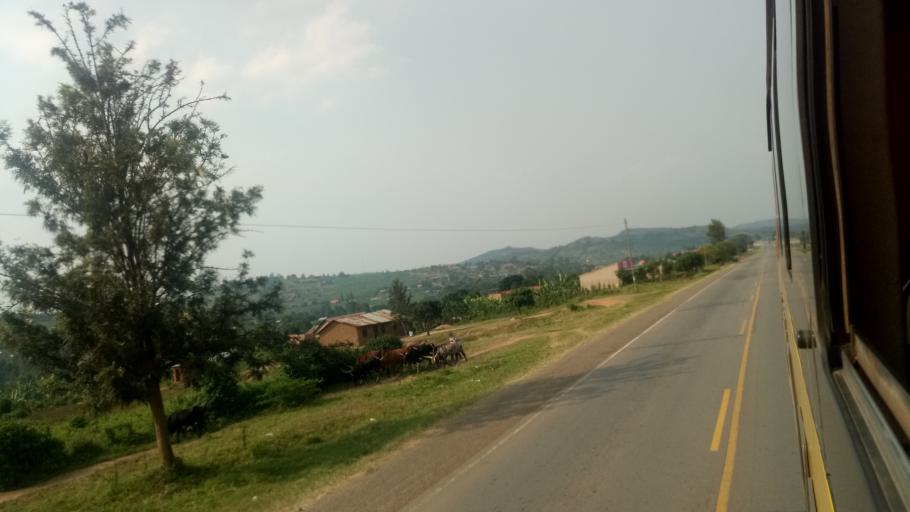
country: UG
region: Western Region
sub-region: Mbarara District
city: Mbarara
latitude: -0.5289
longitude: 30.7232
